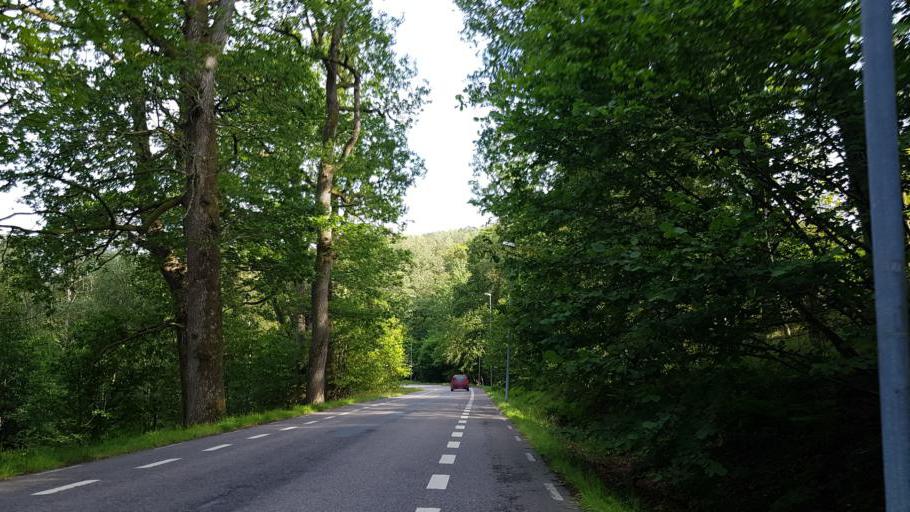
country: SE
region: Vaestra Goetaland
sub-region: Molndal
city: Moelndal
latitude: 57.6617
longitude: 12.0533
